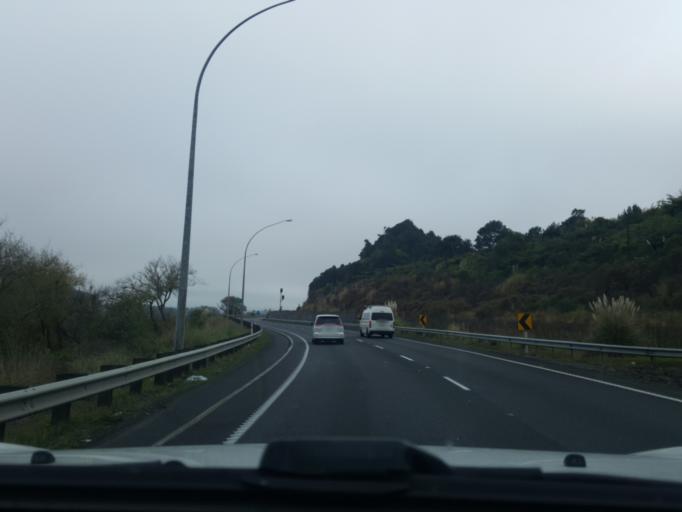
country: NZ
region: Waikato
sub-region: Waikato District
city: Te Kauwhata
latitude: -37.2935
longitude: 175.0589
